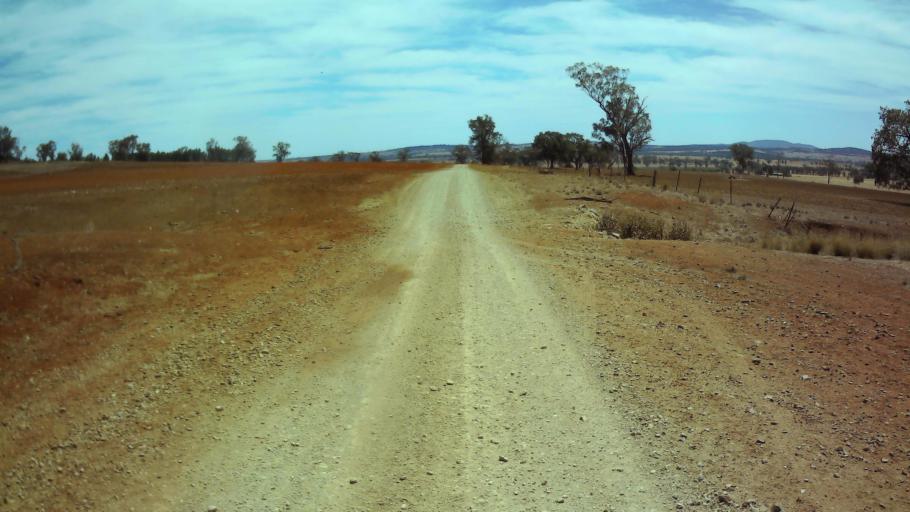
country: AU
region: New South Wales
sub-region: Weddin
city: Grenfell
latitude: -33.7488
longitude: 148.1636
